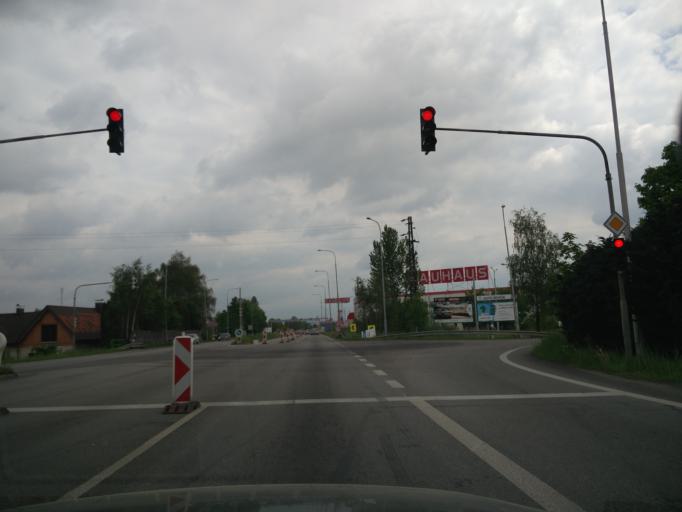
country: CZ
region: Jihocesky
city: Hrdejovice
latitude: 49.0085
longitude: 14.4461
